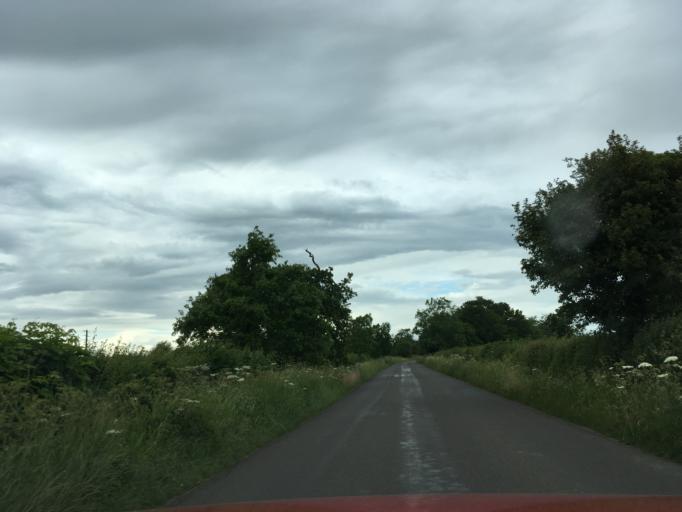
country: GB
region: England
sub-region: Wiltshire
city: Norton
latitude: 51.5929
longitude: -2.1792
